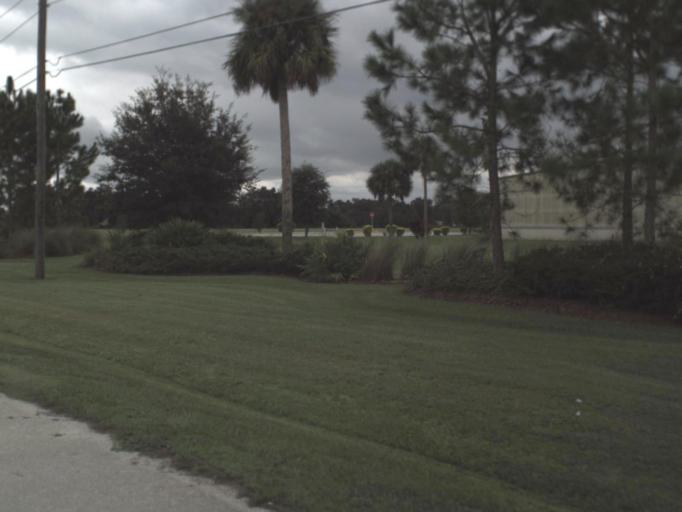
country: US
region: Florida
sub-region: Hardee County
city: Bowling Green
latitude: 27.5949
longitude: -81.8333
